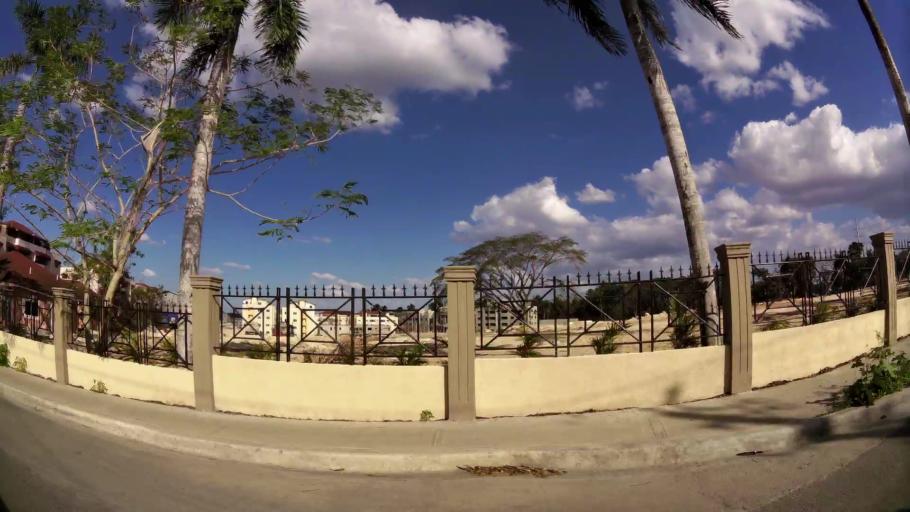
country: DO
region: Nacional
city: Santo Domingo
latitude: 18.5079
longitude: -69.9838
